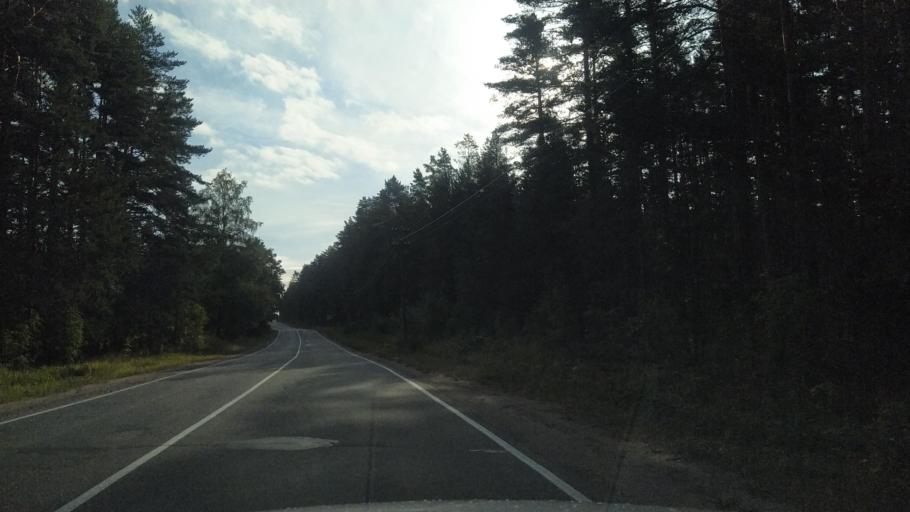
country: RU
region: Leningrad
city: Priozersk
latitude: 61.0017
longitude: 30.2033
